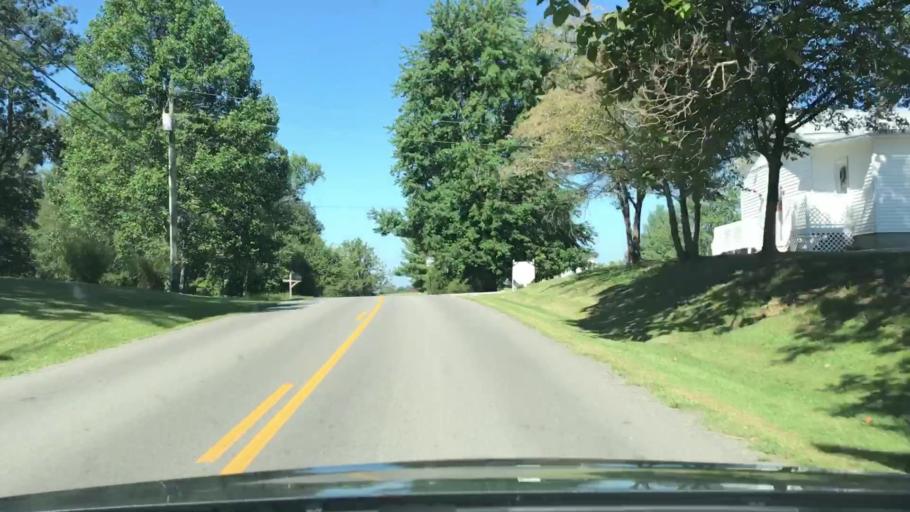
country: US
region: Kentucky
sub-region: Hardin County
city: Elizabethtown
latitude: 37.6014
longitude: -85.8842
